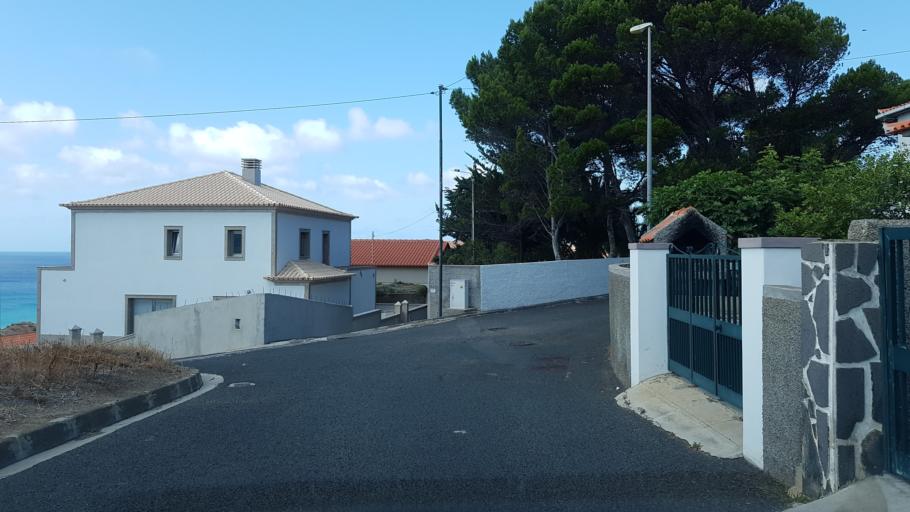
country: PT
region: Madeira
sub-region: Porto Santo
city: Vila de Porto Santo
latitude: 33.0652
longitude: -16.3286
